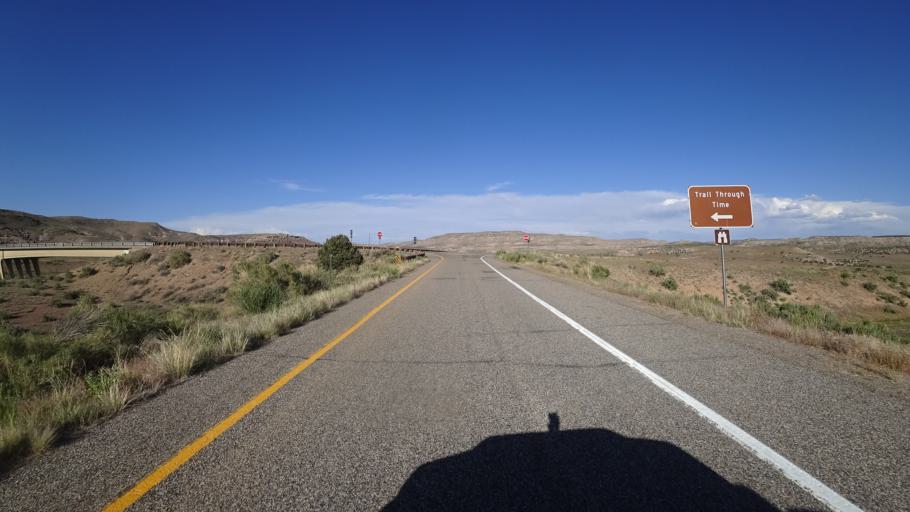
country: US
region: Colorado
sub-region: Mesa County
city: Loma
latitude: 39.1895
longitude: -109.0201
